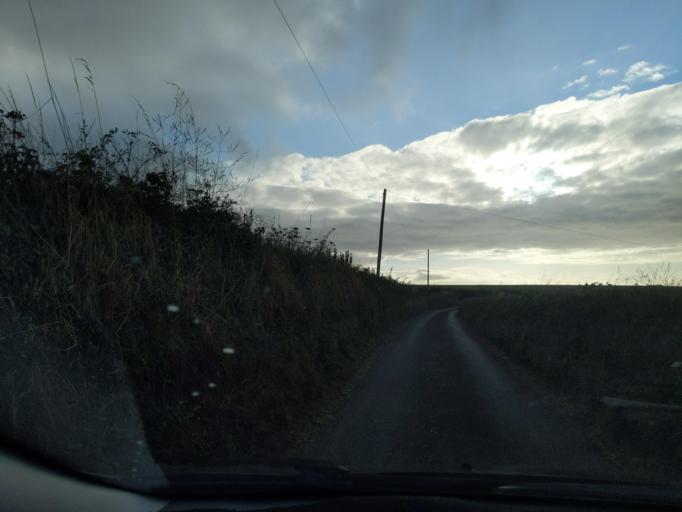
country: GB
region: England
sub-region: Devon
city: Salcombe
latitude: 50.2304
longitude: -3.8119
